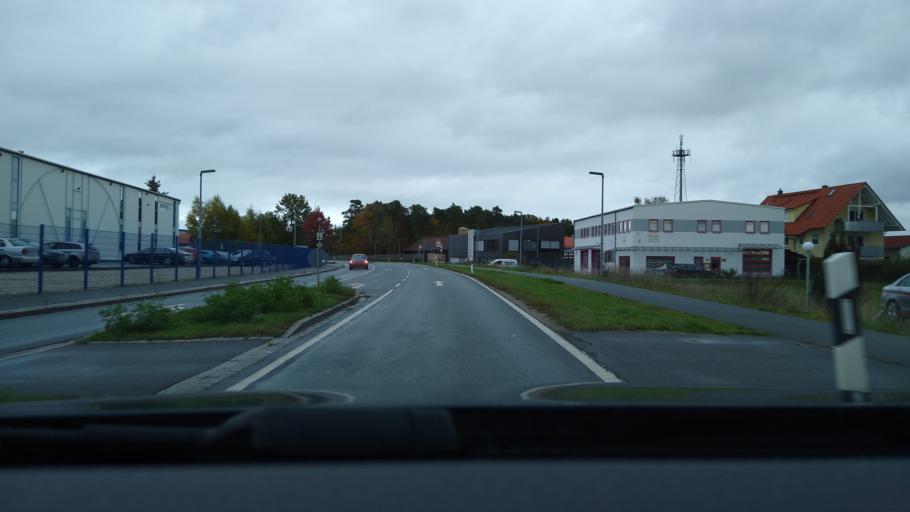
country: DE
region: Bavaria
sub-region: Regierungsbezirk Mittelfranken
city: Hemhofen
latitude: 49.6930
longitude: 10.9437
